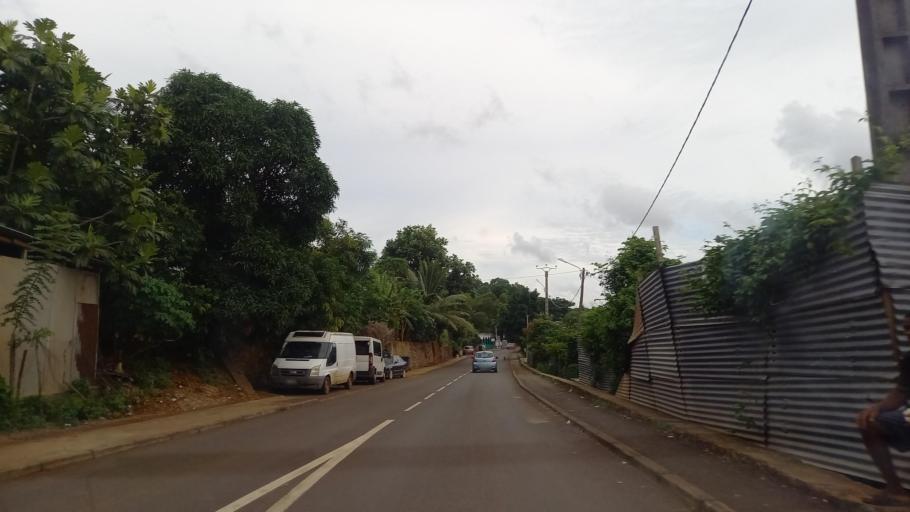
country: YT
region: Chirongui
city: Chirongui
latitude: -12.8920
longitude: 45.1406
